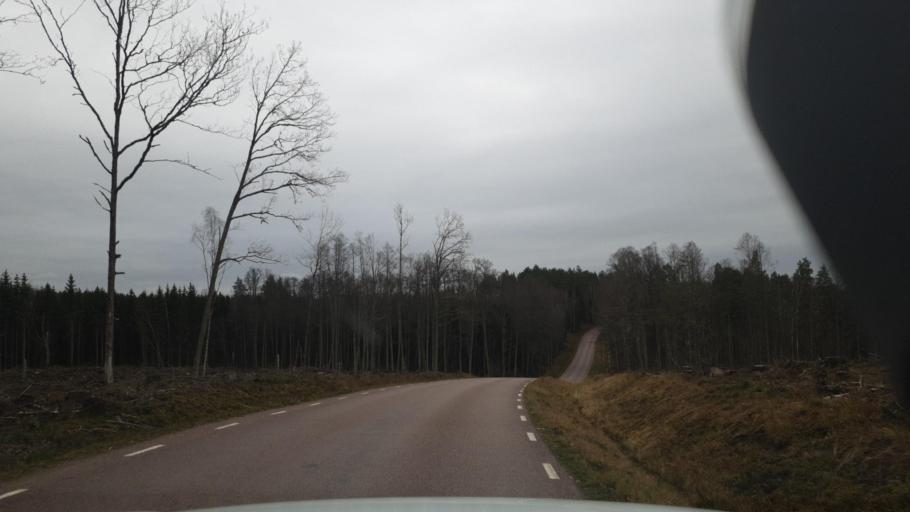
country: SE
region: Vaermland
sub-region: Grums Kommun
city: Grums
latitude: 59.4284
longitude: 13.0856
